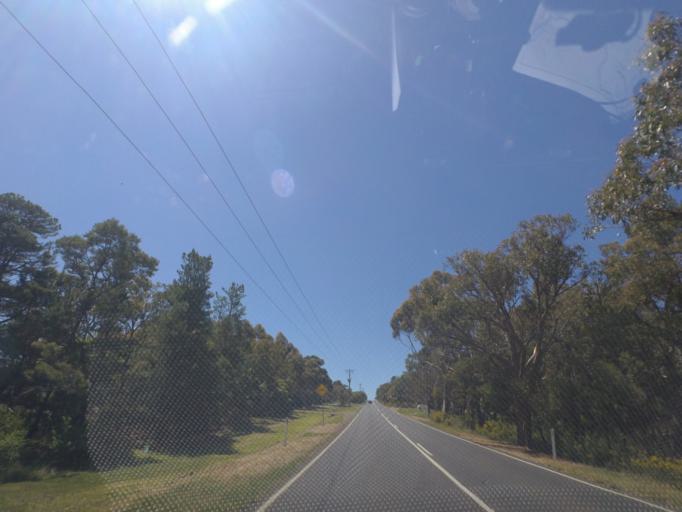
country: AU
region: Victoria
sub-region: Hume
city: Sunbury
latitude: -37.4523
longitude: 144.6899
